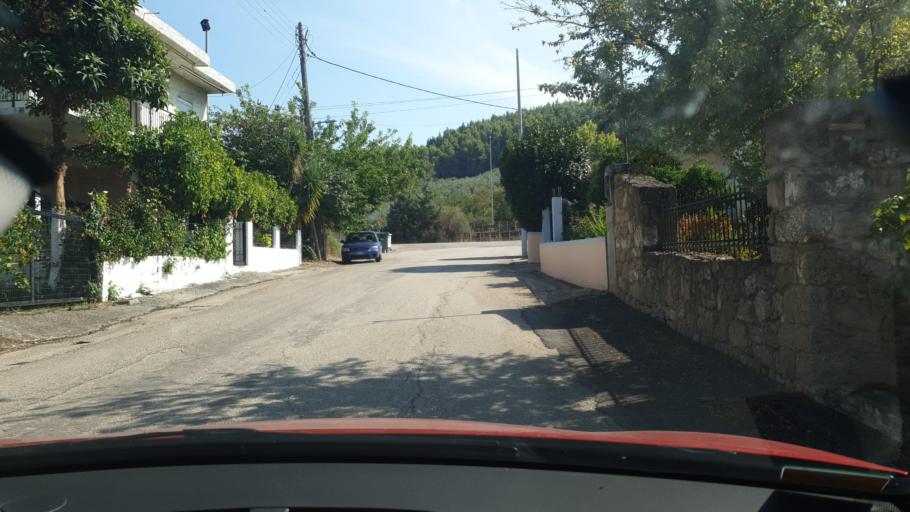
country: GR
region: Central Greece
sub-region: Nomos Fthiotidos
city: Livanates
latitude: 38.7400
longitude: 23.0345
